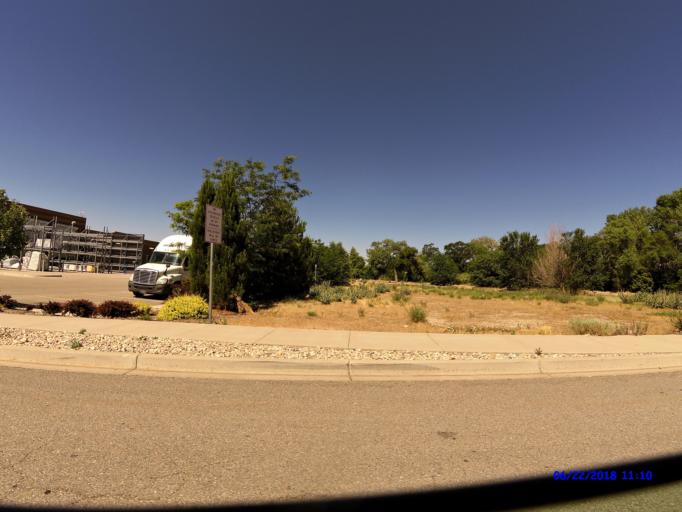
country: US
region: Utah
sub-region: Weber County
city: Ogden
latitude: 41.2333
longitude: -111.9805
